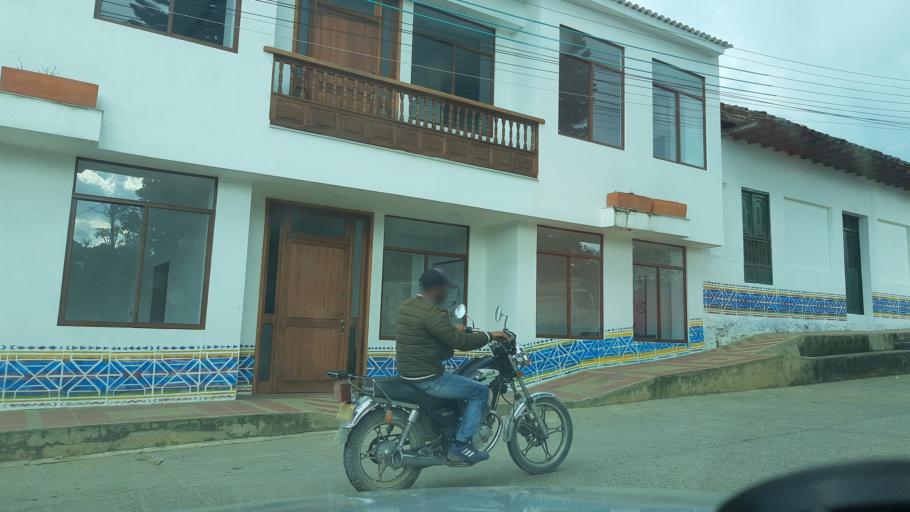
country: CO
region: Boyaca
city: Santa Sofia
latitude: 5.7525
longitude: -73.5492
